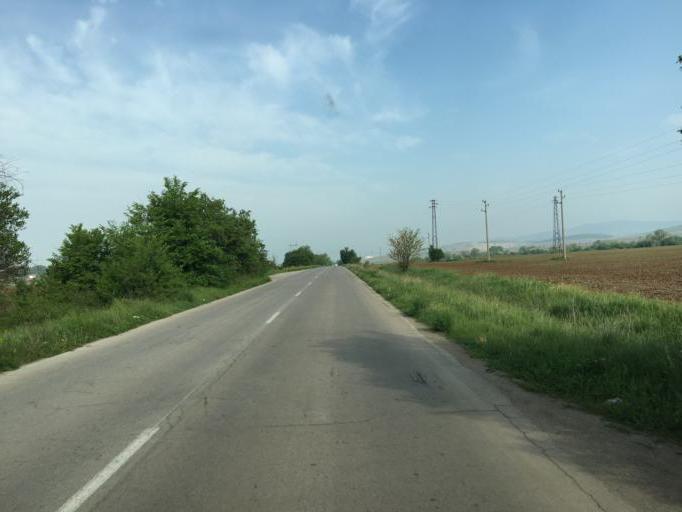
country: BG
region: Pernik
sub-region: Obshtina Radomir
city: Radomir
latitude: 42.4820
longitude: 23.0572
